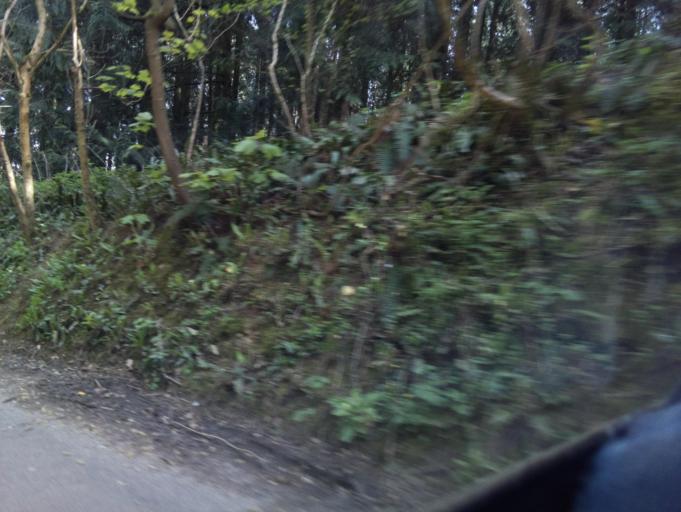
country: GB
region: England
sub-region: Dorset
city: Sherborne
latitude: 50.9727
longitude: -2.5328
